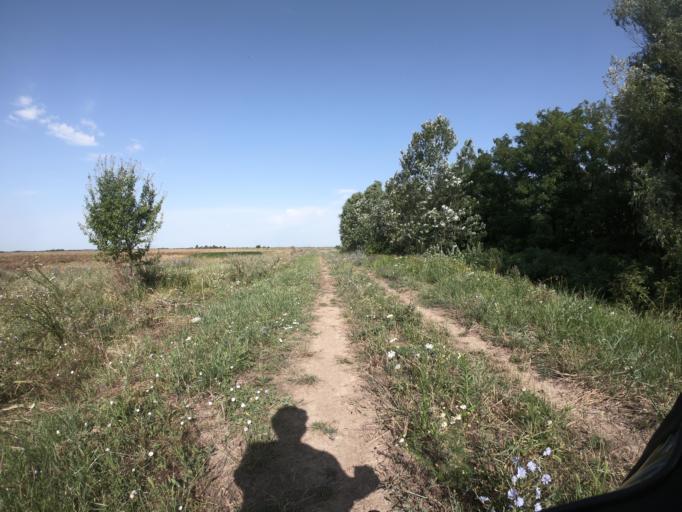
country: HU
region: Hajdu-Bihar
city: Egyek
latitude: 47.5784
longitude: 20.9241
